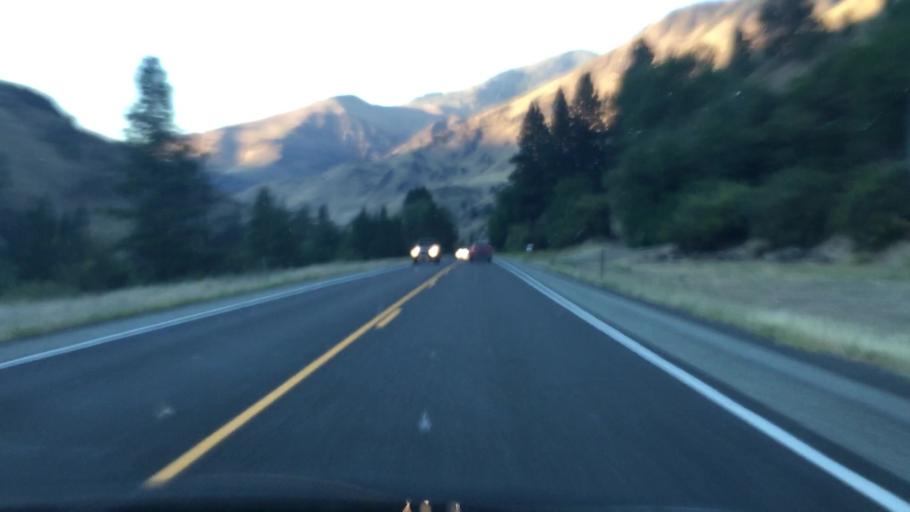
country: US
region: Idaho
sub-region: Valley County
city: McCall
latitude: 45.3112
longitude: -116.3587
